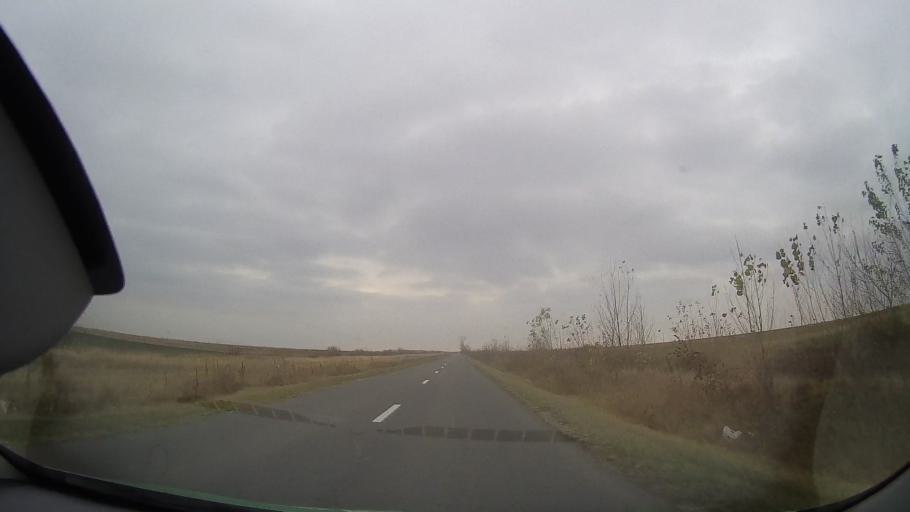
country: RO
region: Ialomita
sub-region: Comuna Garbovi
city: Garbovi
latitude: 44.7660
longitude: 26.7382
